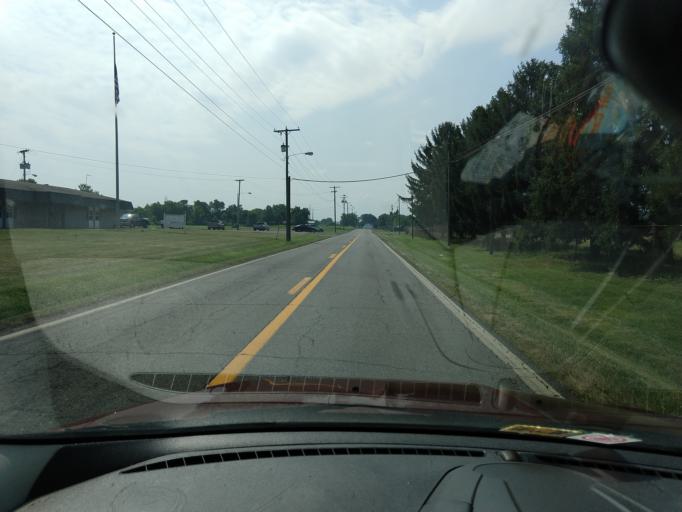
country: US
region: West Virginia
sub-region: Mason County
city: New Haven
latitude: 38.9590
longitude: -81.9245
